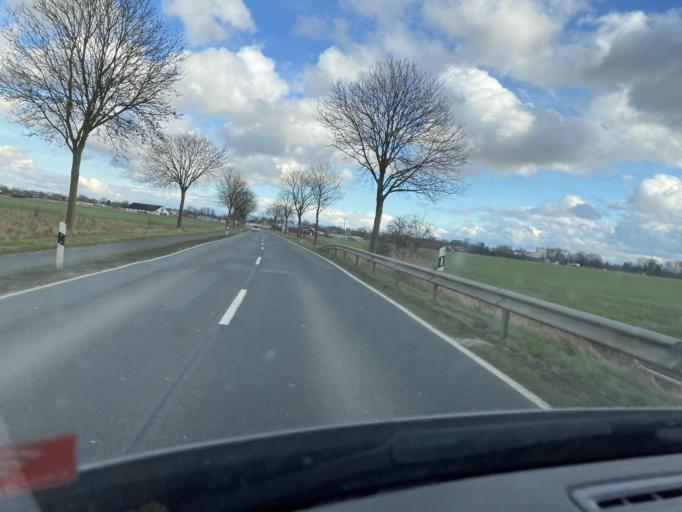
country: DE
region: Lower Saxony
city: Sande
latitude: 53.4894
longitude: 8.0166
